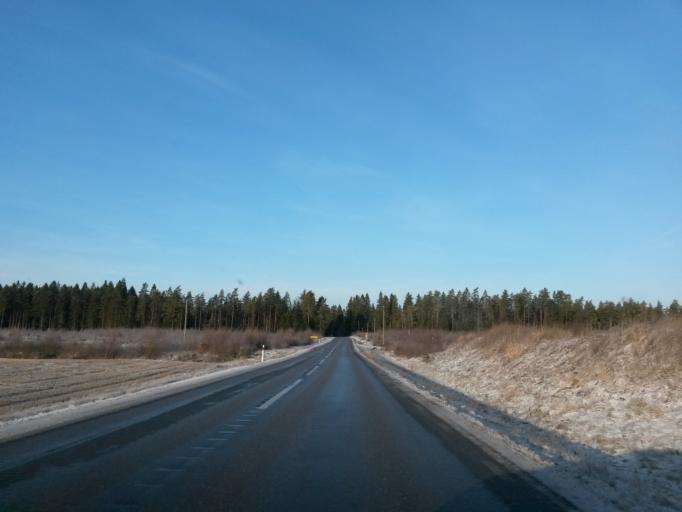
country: SE
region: Vaestra Goetaland
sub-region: Essunga Kommun
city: Nossebro
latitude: 58.1020
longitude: 12.6558
